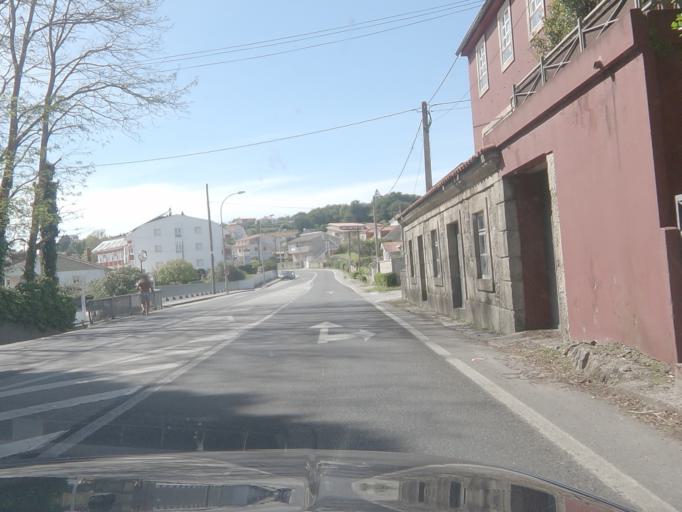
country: ES
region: Galicia
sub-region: Provincia de Pontevedra
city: Sanxenxo
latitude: 42.3981
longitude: -8.7862
